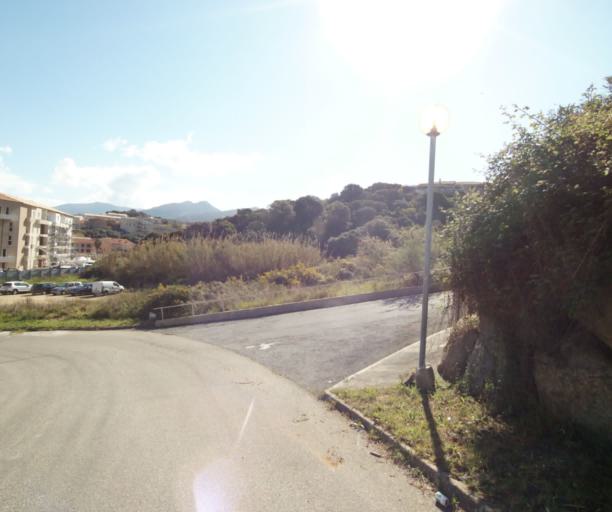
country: FR
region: Corsica
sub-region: Departement de la Corse-du-Sud
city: Propriano
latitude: 41.6722
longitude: 8.9006
